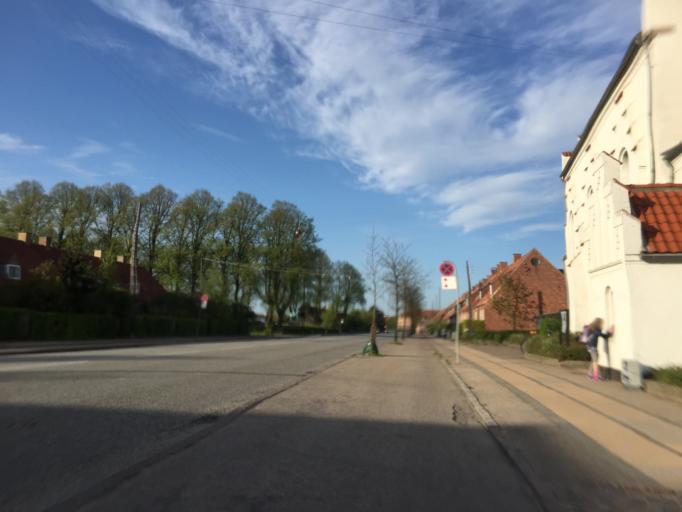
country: DK
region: Capital Region
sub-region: Kobenhavn
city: Vanlose
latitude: 55.6958
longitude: 12.5120
